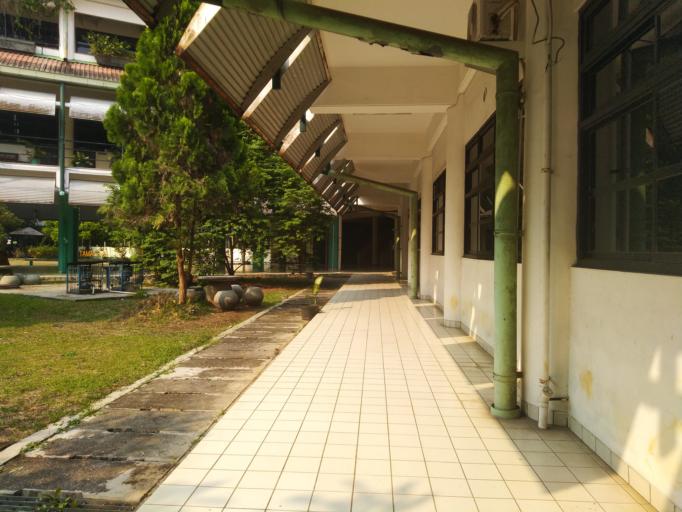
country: ID
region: West Java
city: Ciampea
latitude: -6.5592
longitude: 106.7290
